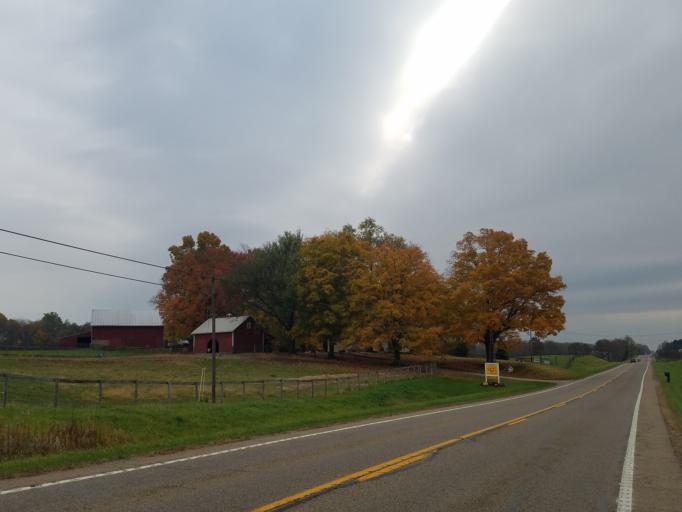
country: US
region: Ohio
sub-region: Morrow County
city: Mount Gilead
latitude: 40.5312
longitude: -82.7636
